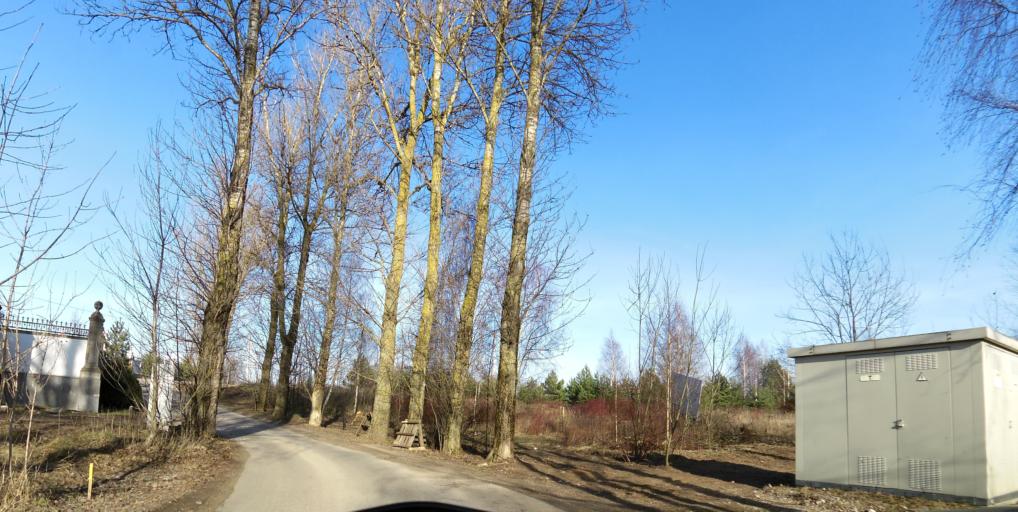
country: LT
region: Vilnius County
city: Pilaite
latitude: 54.7068
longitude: 25.1601
